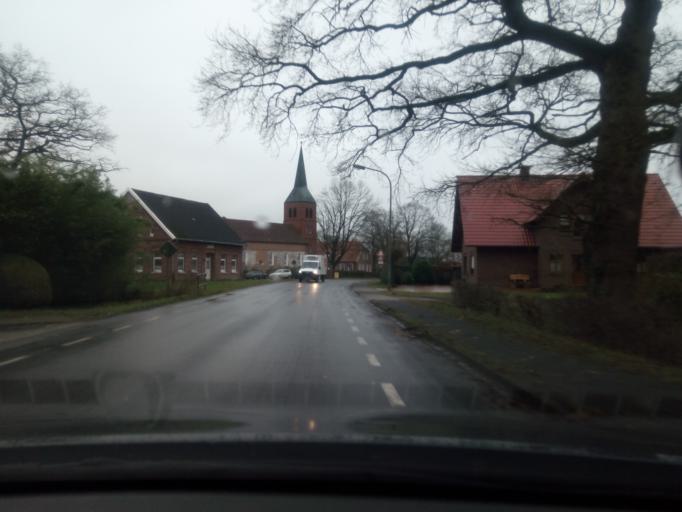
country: DE
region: Lower Saxony
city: Nortmoor
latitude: 53.2490
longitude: 7.5211
